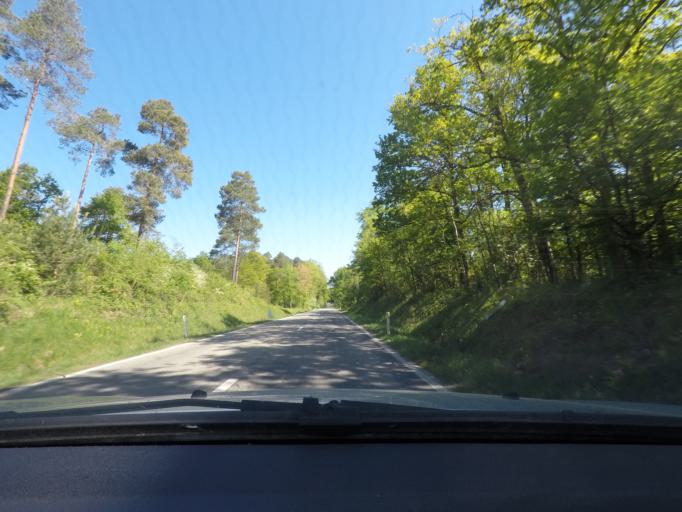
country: BE
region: Wallonia
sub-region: Province du Luxembourg
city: Wellin
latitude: 50.1768
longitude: 5.1187
